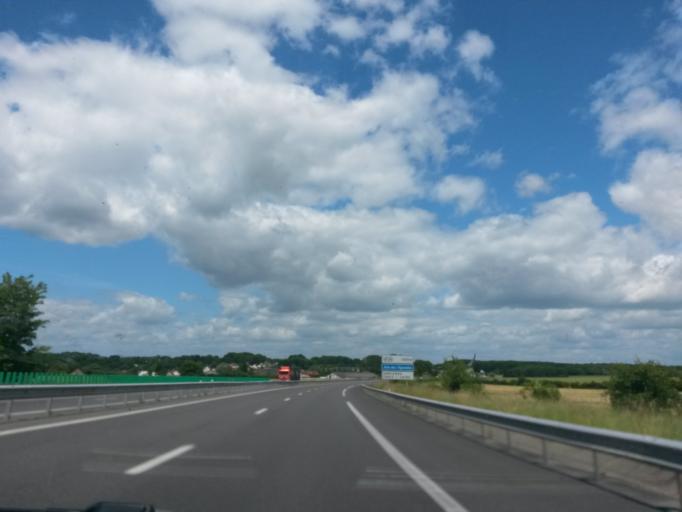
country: FR
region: Bourgogne
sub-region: Departement de la Nievre
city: Pouilly-sur-Loire
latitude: 47.3279
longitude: 2.9309
